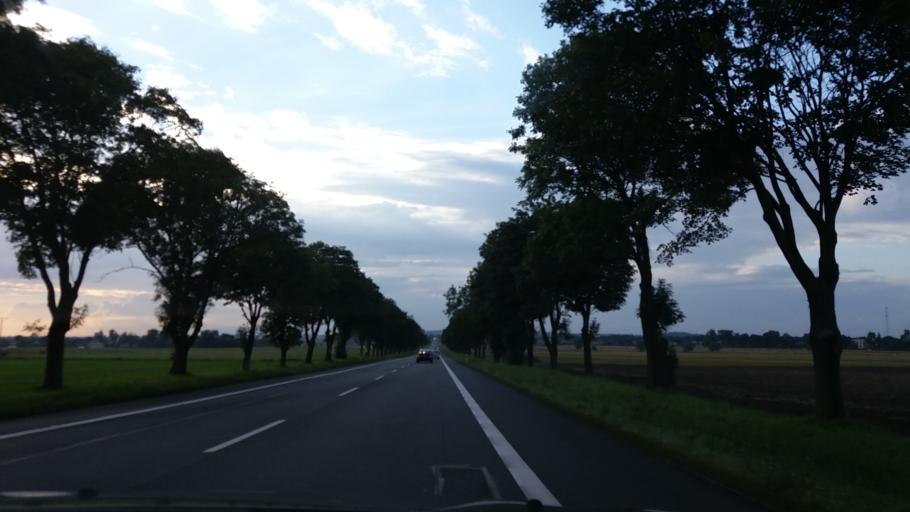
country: PL
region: Lower Silesian Voivodeship
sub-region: Powiat polkowicki
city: Radwanice
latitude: 51.6097
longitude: 15.9426
